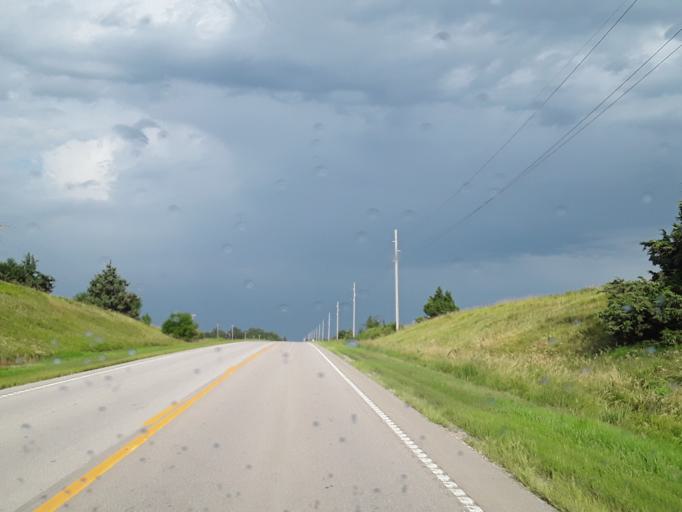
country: US
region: Nebraska
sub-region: Saunders County
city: Ashland
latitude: 41.0887
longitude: -96.4121
